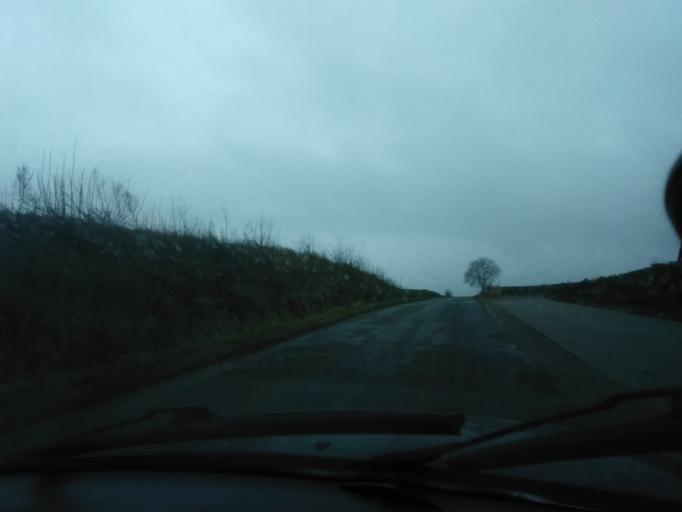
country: PL
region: Subcarpathian Voivodeship
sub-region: Powiat jaroslawski
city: Rokietnica
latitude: 49.9126
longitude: 22.6113
